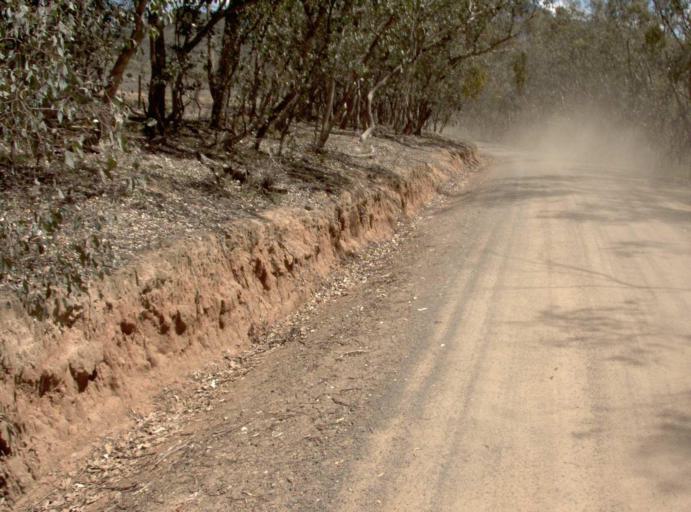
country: AU
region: New South Wales
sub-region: Snowy River
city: Jindabyne
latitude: -37.0689
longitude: 148.4988
